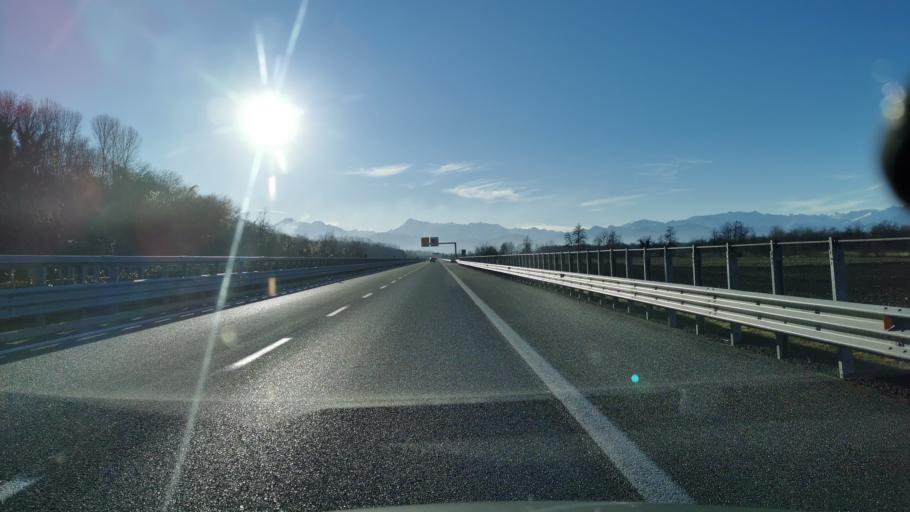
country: IT
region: Piedmont
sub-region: Provincia di Cuneo
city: Castelletto Stura
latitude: 44.4402
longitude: 7.6269
